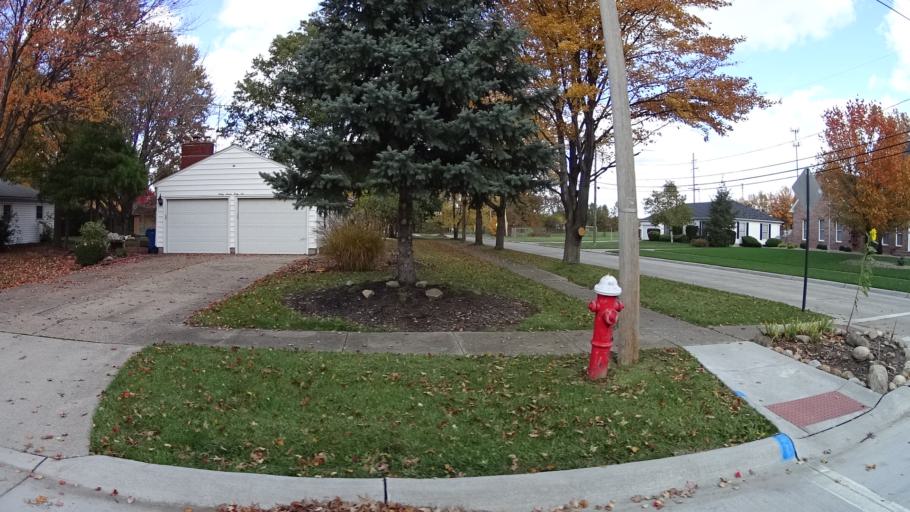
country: US
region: Ohio
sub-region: Lorain County
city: Lorain
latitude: 41.4360
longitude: -82.1795
